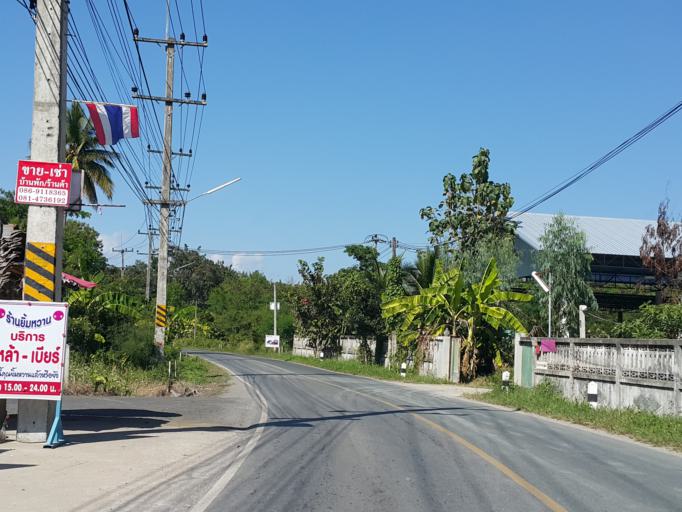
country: TH
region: Chiang Mai
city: San Sai
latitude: 18.9524
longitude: 98.9248
